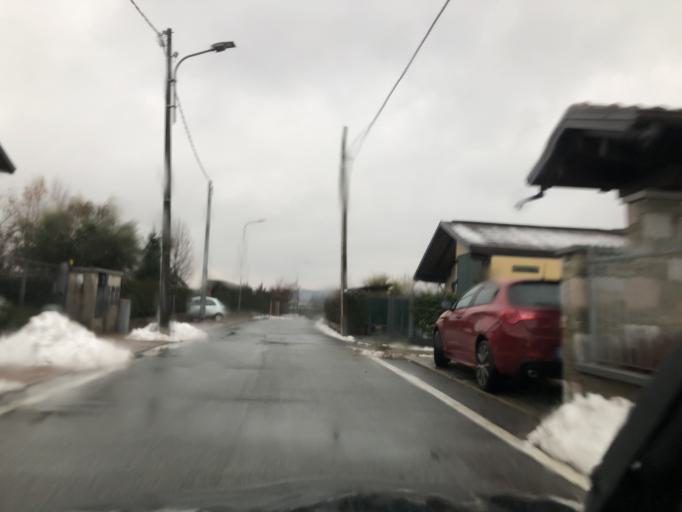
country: IT
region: Piedmont
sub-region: Provincia di Novara
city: Oleggio Castello
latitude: 45.7540
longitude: 8.5261
